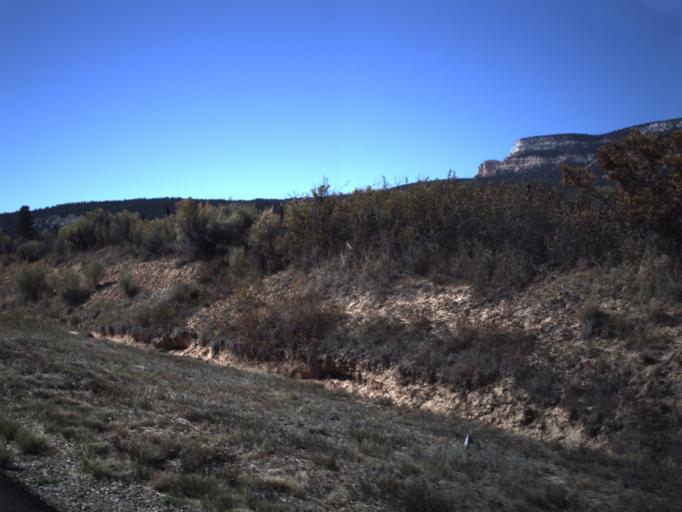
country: US
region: Utah
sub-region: Garfield County
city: Panguitch
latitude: 37.6773
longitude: -111.8215
